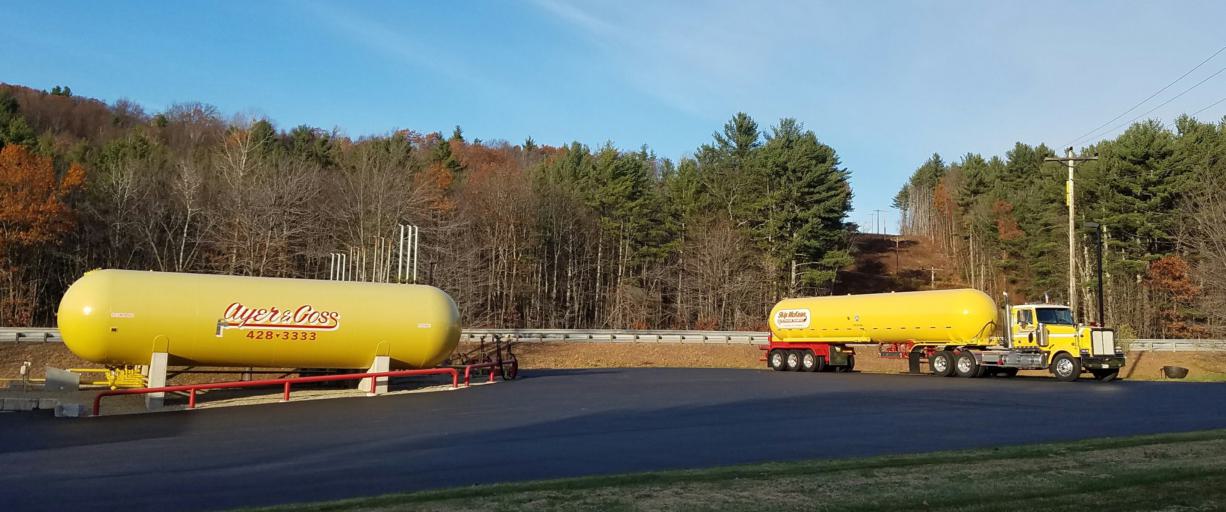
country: US
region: New Hampshire
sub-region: Merrimack County
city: Henniker
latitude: 43.1843
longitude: -71.7912
